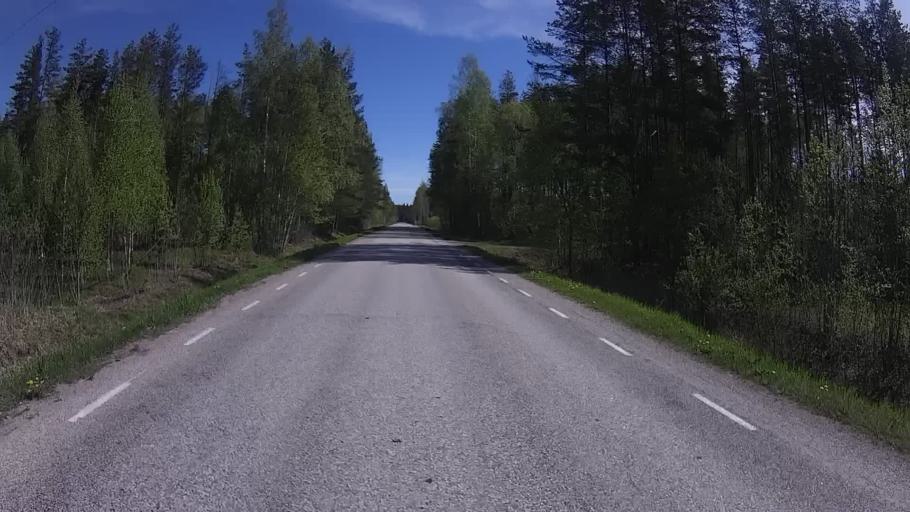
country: EE
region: Polvamaa
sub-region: Raepina vald
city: Rapina
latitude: 57.9737
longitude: 27.5632
